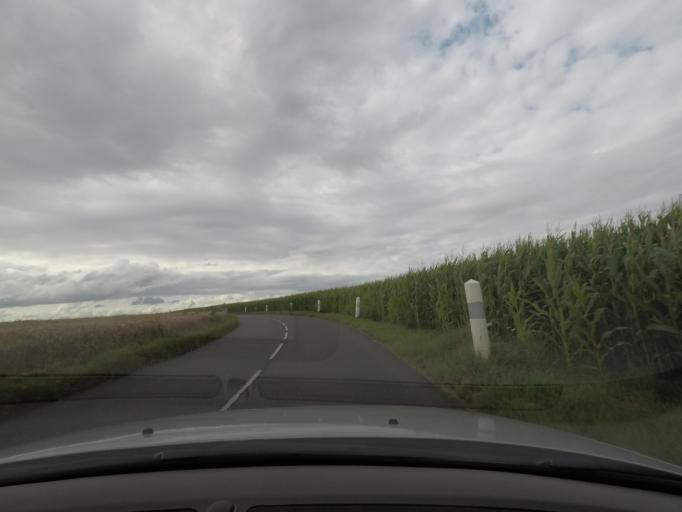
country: FR
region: Haute-Normandie
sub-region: Departement de la Seine-Maritime
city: Ymare
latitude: 49.3393
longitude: 1.1904
